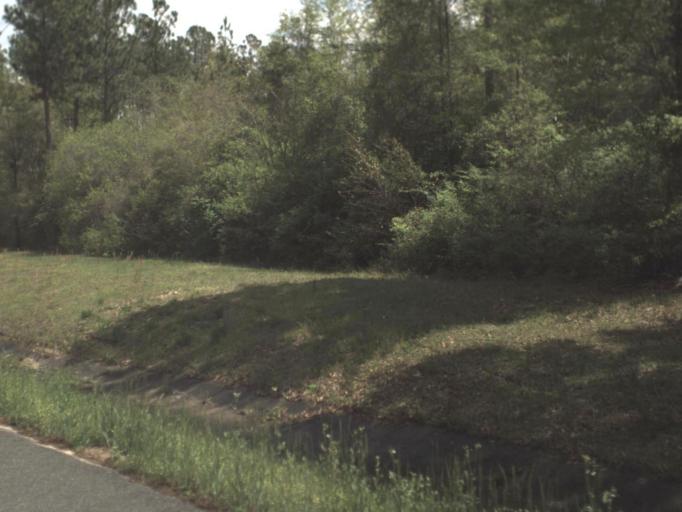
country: US
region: Florida
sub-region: Okaloosa County
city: Crestview
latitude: 30.8614
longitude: -86.6727
